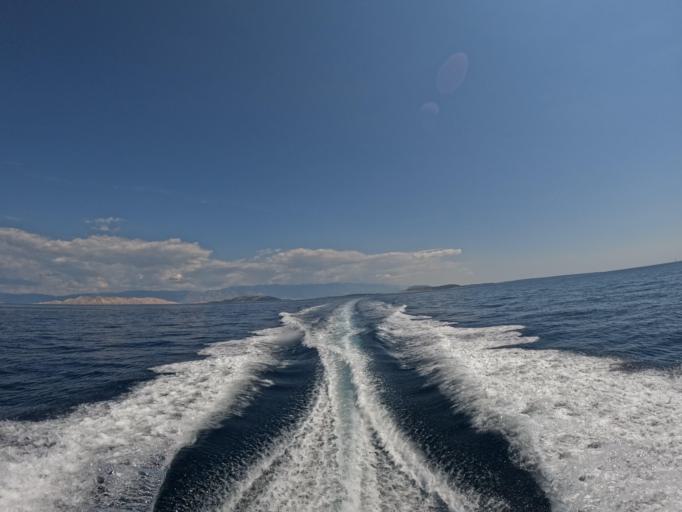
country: HR
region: Primorsko-Goranska
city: Lopar
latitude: 44.8921
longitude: 14.6306
